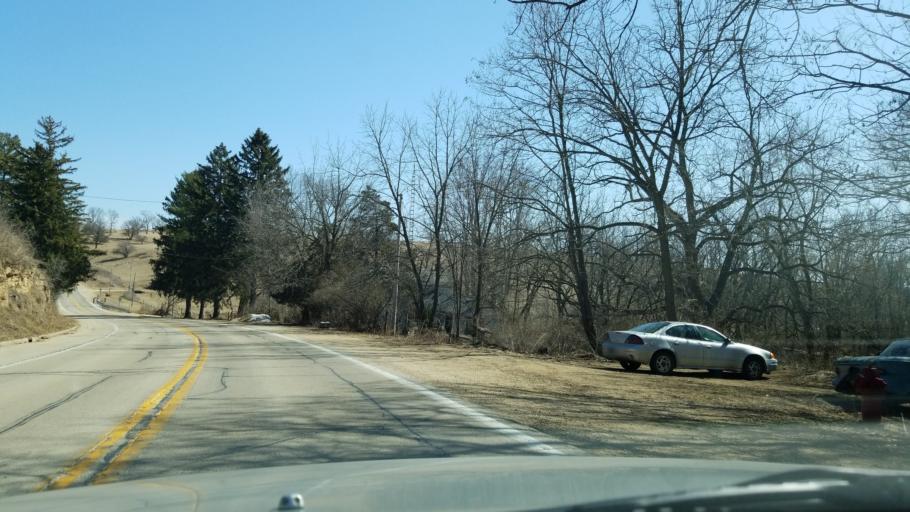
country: US
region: Wisconsin
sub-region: Iowa County
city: Mineral Point
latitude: 42.9146
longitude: -90.2695
